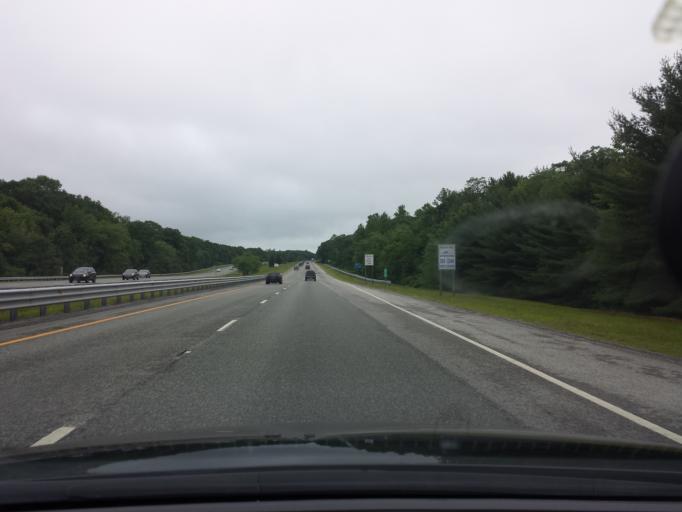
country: US
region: Rhode Island
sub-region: Washington County
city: Hope Valley
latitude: 41.5426
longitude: -71.6765
